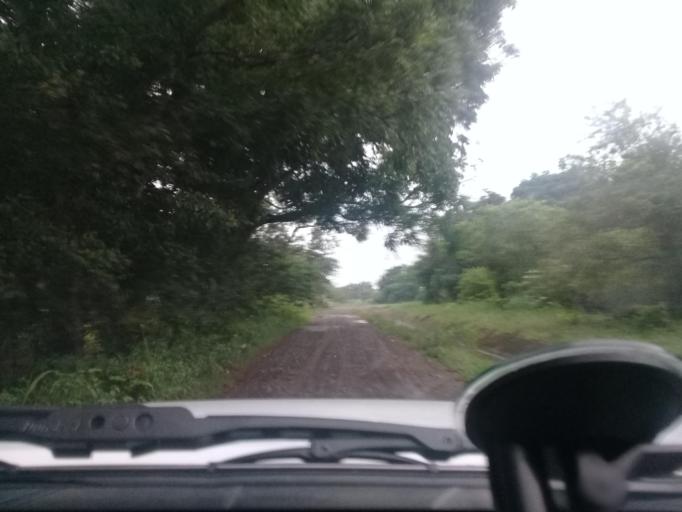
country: MX
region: Veracruz
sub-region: La Antigua
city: Nicolas Blanco (San Pancho)
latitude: 19.3510
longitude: -96.3430
